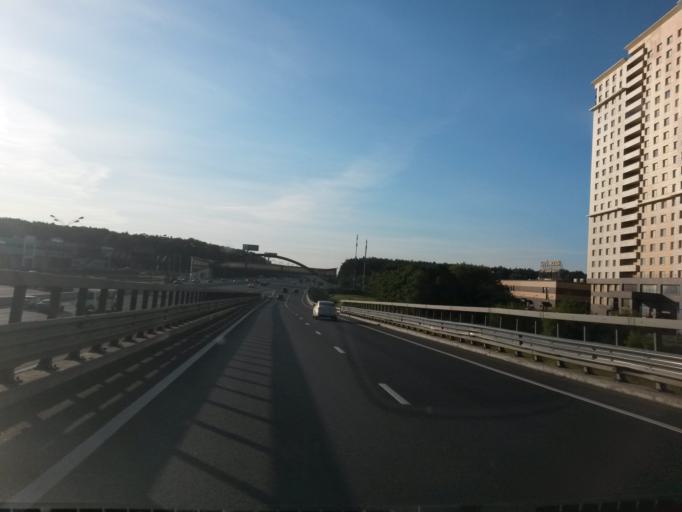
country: RU
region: Moscow
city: Babushkin
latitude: 55.8801
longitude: 37.7295
